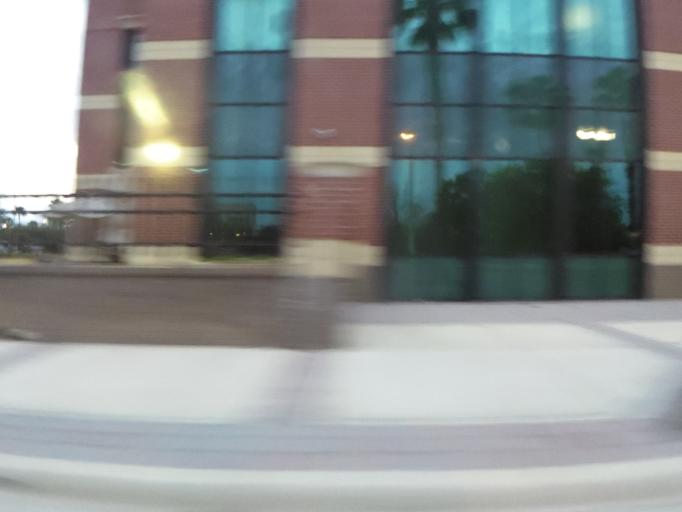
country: US
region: Florida
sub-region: Duval County
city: Jacksonville
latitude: 30.3334
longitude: -81.6677
